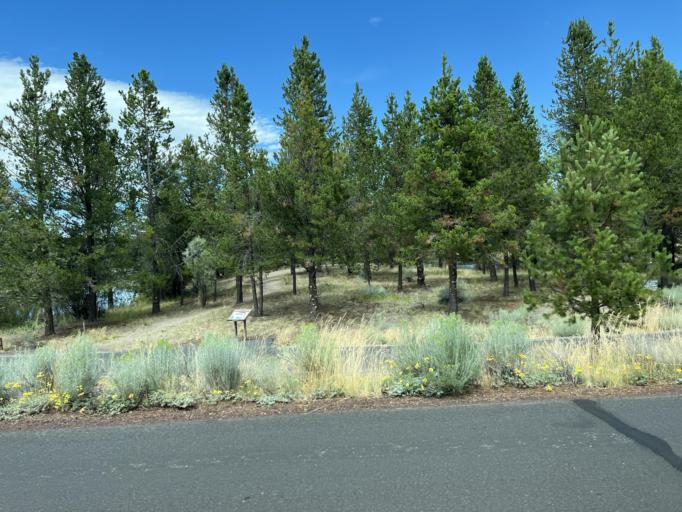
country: US
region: Oregon
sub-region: Deschutes County
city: Sunriver
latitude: 43.8830
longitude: -121.4452
